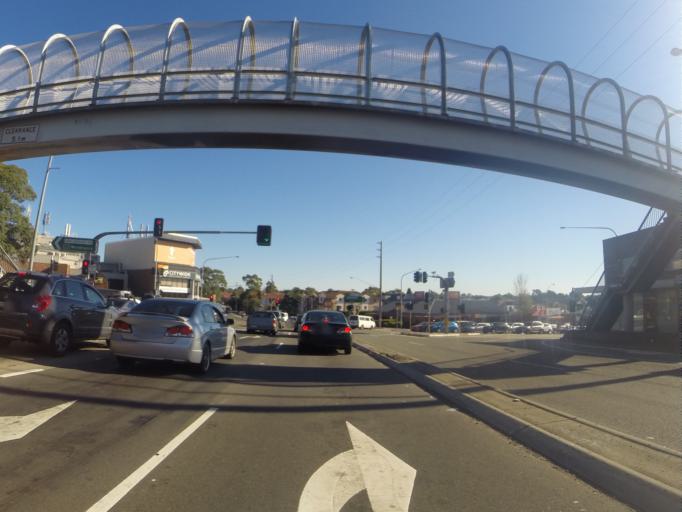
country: AU
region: New South Wales
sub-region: Hurstville
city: Penshurst
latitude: -33.9525
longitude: 151.0840
